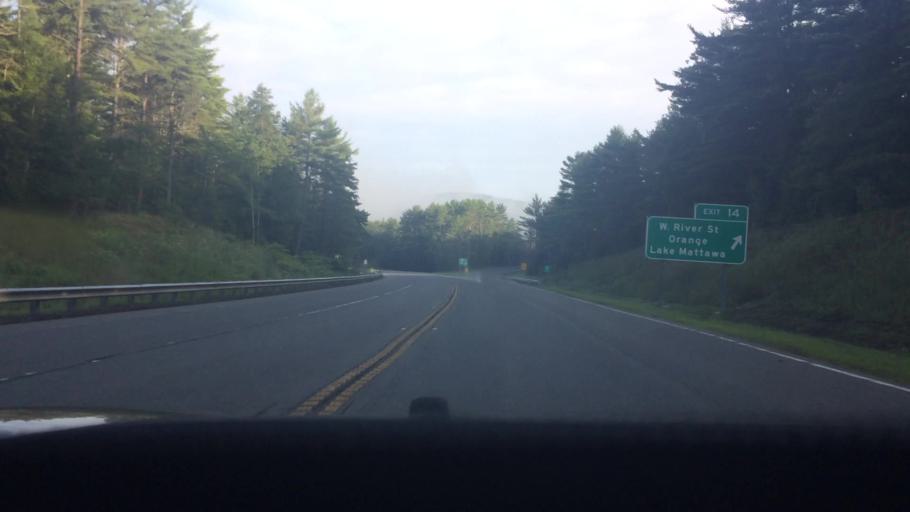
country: US
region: Massachusetts
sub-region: Franklin County
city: Orange
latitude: 42.5870
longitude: -72.3275
